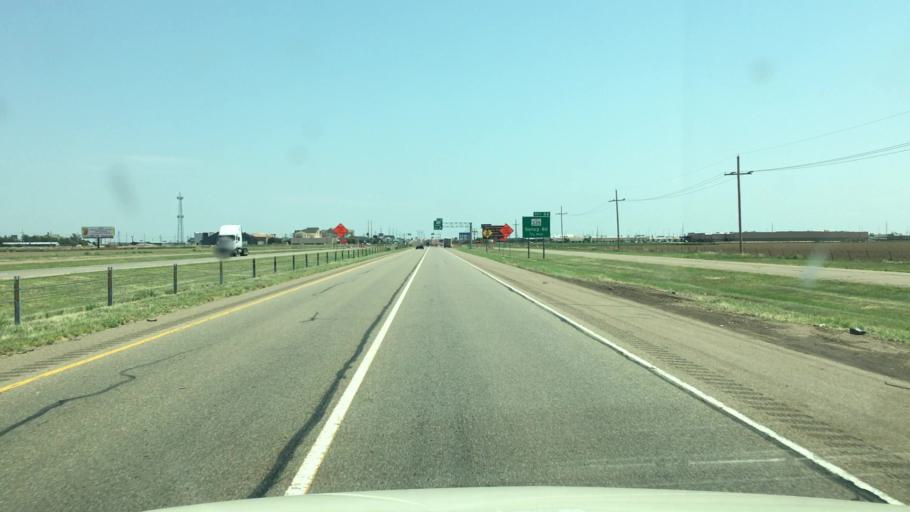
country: US
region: Texas
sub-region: Potter County
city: Bushland
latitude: 35.1873
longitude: -101.9514
